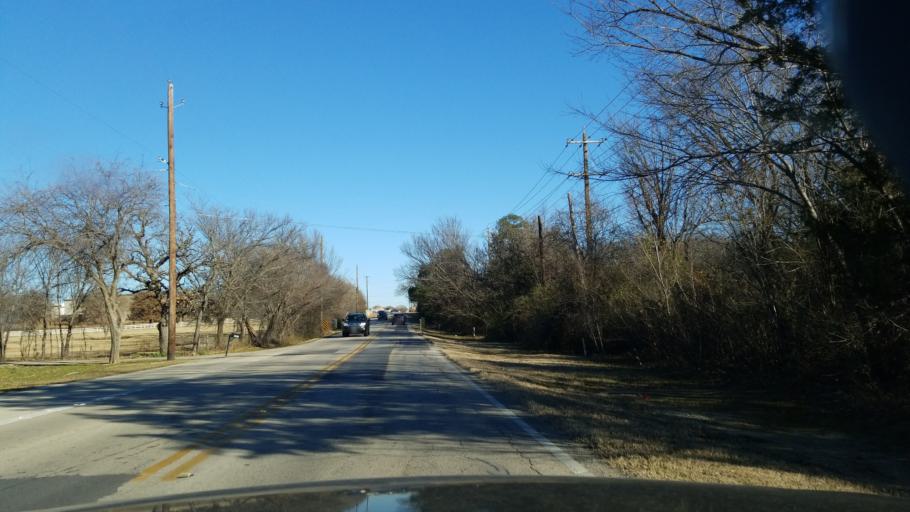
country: US
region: Texas
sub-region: Denton County
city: Corinth
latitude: 33.1471
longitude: -97.1106
